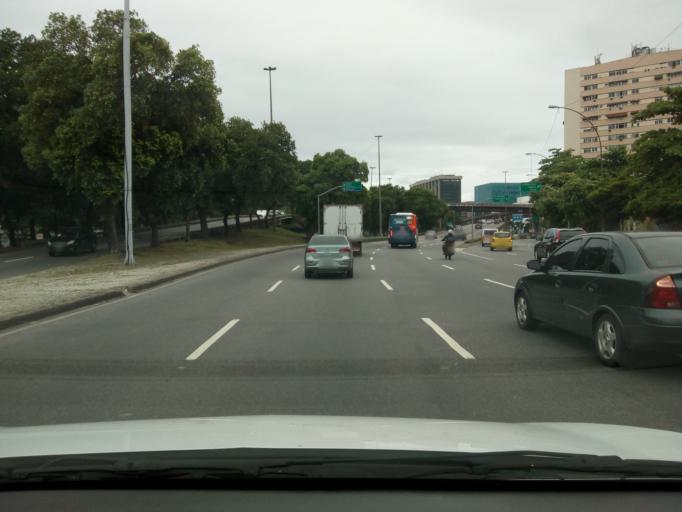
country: BR
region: Rio de Janeiro
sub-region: Rio De Janeiro
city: Rio de Janeiro
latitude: -22.9109
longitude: -43.2124
